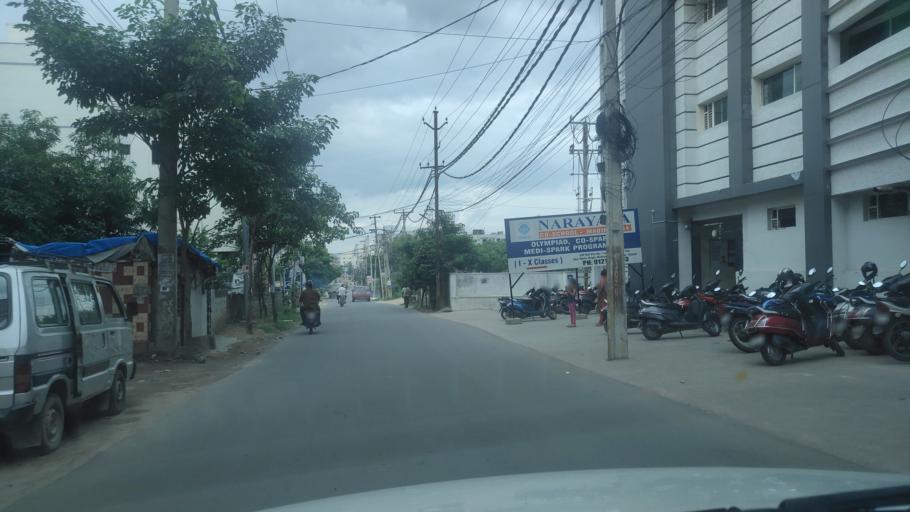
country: IN
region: Telangana
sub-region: Medak
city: Serilingampalle
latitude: 17.4956
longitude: 78.3483
